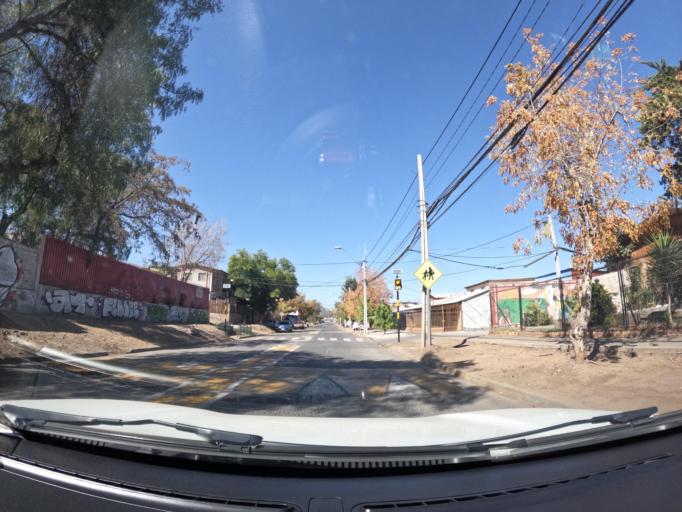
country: CL
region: Santiago Metropolitan
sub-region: Provincia de Santiago
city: Villa Presidente Frei, Nunoa, Santiago, Chile
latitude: -33.4732
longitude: -70.5391
